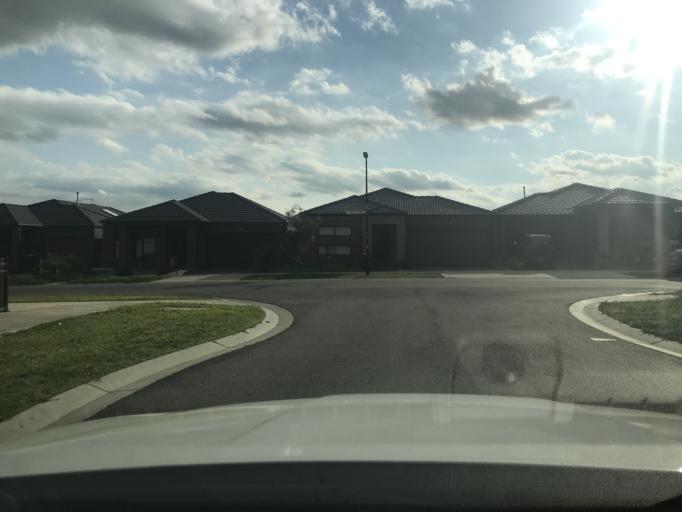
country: AU
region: Victoria
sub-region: Hume
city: Craigieburn
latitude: -37.5774
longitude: 144.9030
